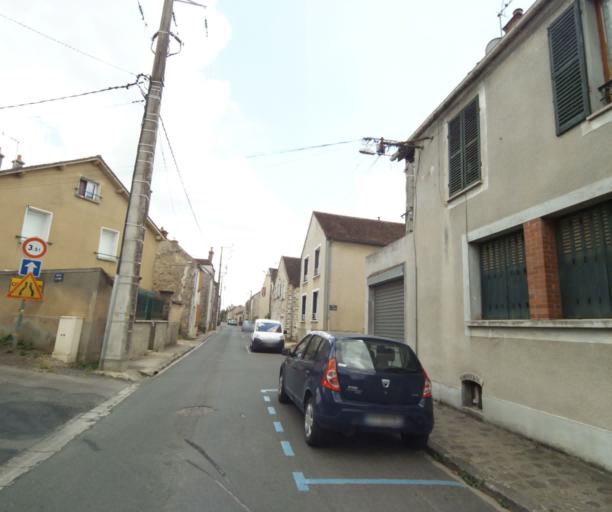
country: FR
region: Ile-de-France
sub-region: Departement de Seine-et-Marne
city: Hericy
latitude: 48.4467
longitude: 2.7750
